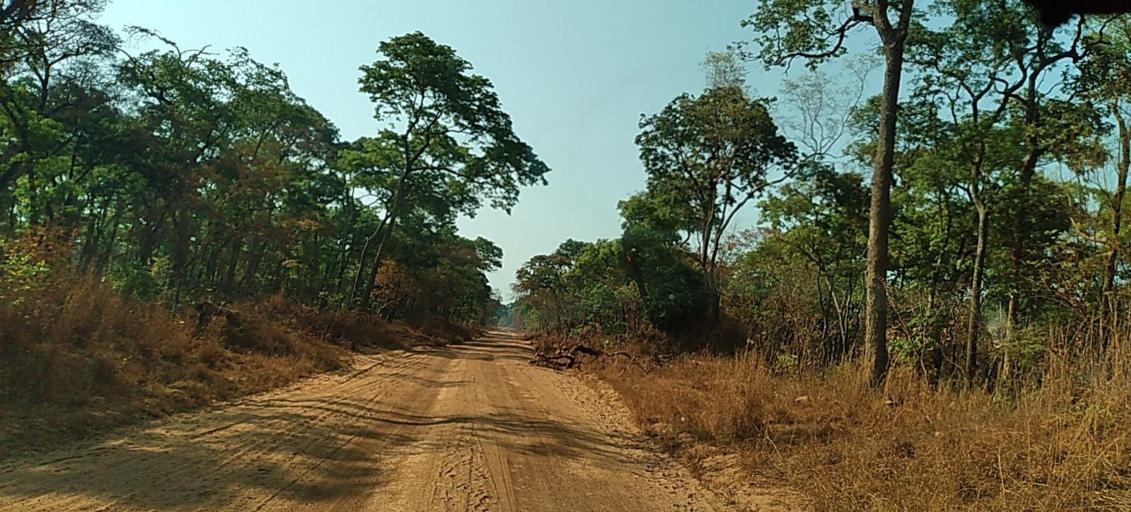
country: ZM
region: North-Western
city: Kasempa
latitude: -13.6443
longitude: 25.9992
